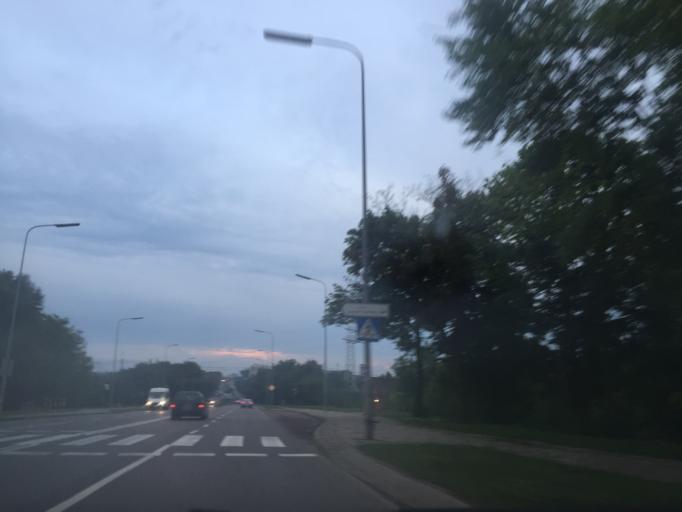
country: PL
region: Podlasie
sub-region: Bialystok
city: Bialystok
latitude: 53.1438
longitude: 23.0856
